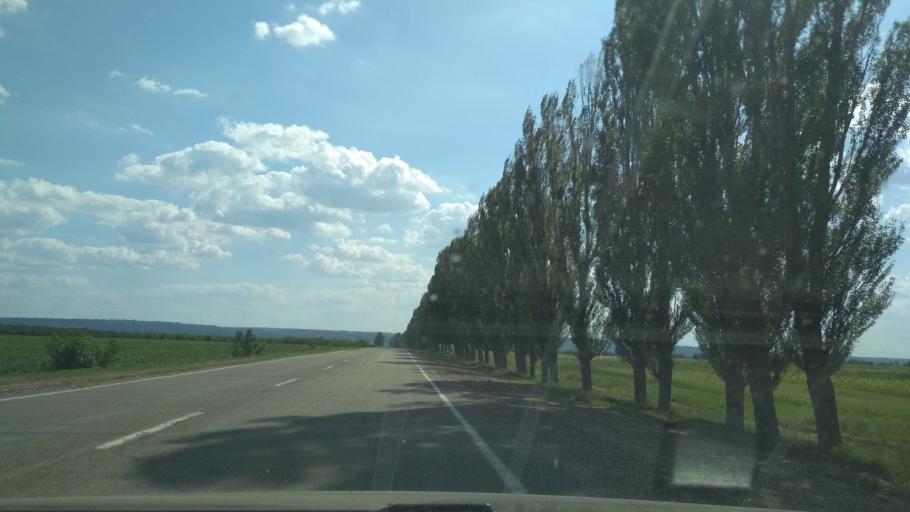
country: MD
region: Chisinau
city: Vadul lui Voda
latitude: 47.1310
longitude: 29.1258
